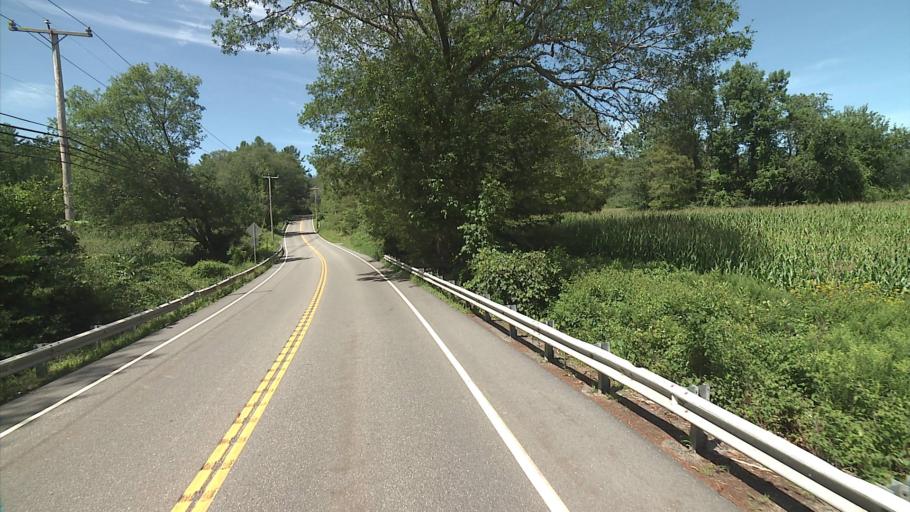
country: US
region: Connecticut
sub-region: Windham County
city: South Woodstock
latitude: 41.8879
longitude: -72.0783
